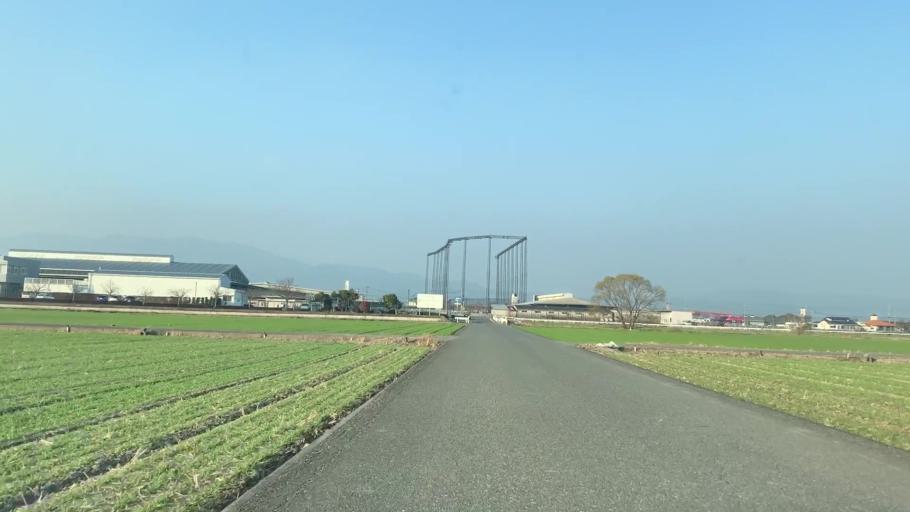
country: JP
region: Saga Prefecture
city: Saga-shi
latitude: 33.2616
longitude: 130.2481
